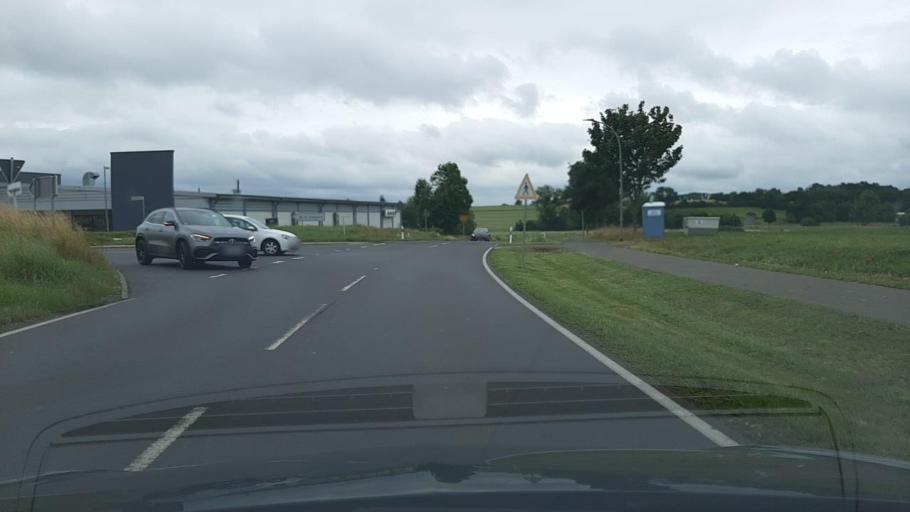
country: DE
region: Rheinland-Pfalz
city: Polch
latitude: 50.3037
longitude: 7.3267
